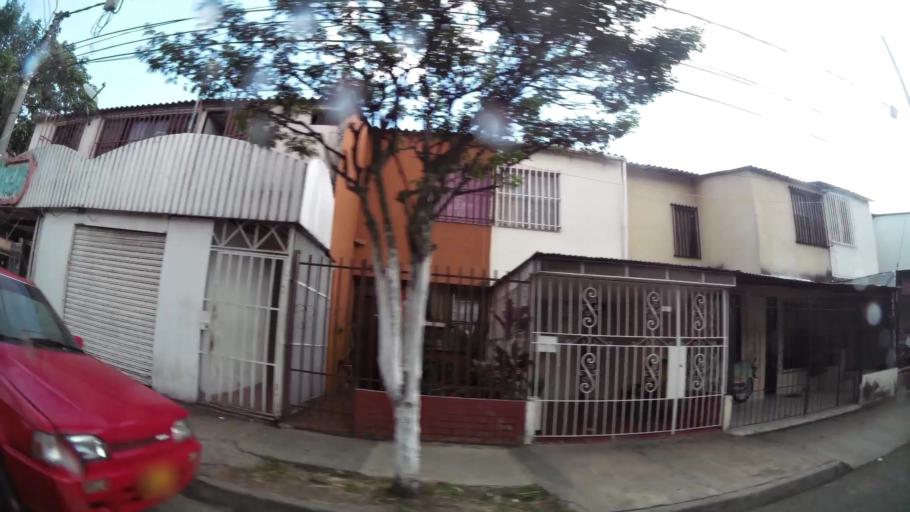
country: CO
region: Valle del Cauca
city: Cali
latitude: 3.4683
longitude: -76.4874
